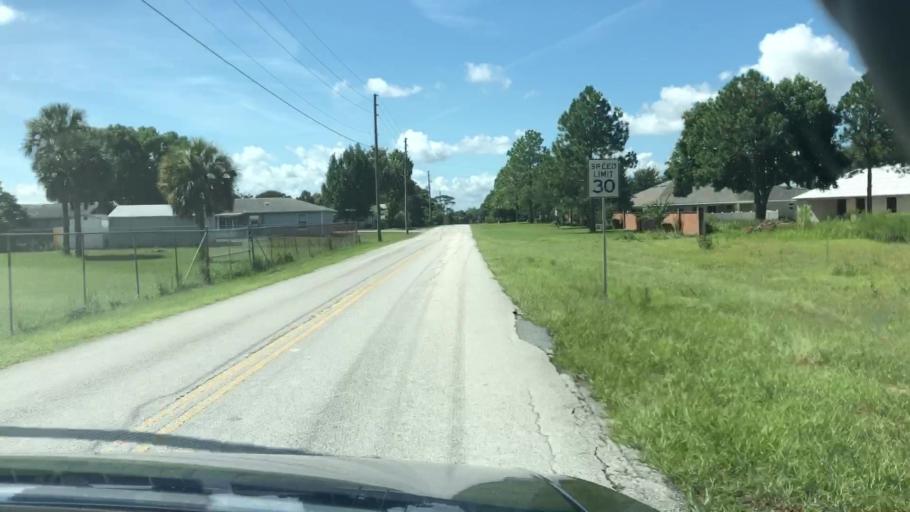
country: US
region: Florida
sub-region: Lake County
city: Eustis
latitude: 28.8814
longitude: -81.7371
